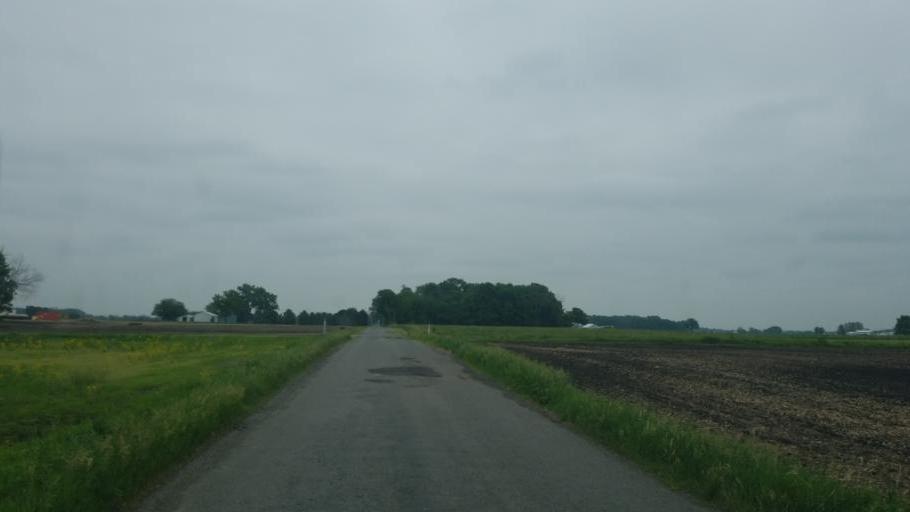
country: US
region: Indiana
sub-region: Marshall County
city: Bremen
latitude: 41.4935
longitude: -86.1137
